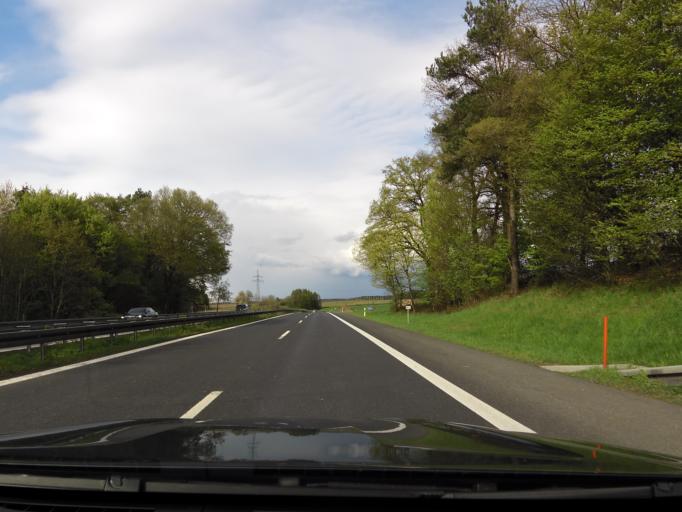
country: DE
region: Bavaria
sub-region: Upper Bavaria
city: Wolnzach
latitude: 48.6056
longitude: 11.6521
